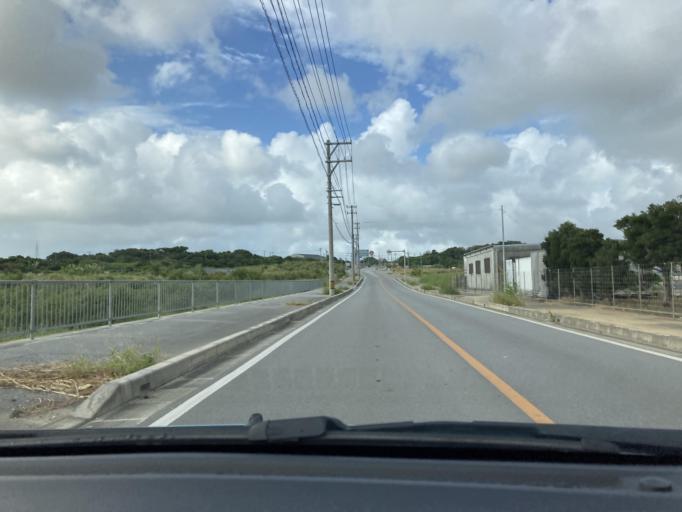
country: JP
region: Okinawa
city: Itoman
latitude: 26.1153
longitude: 127.6920
